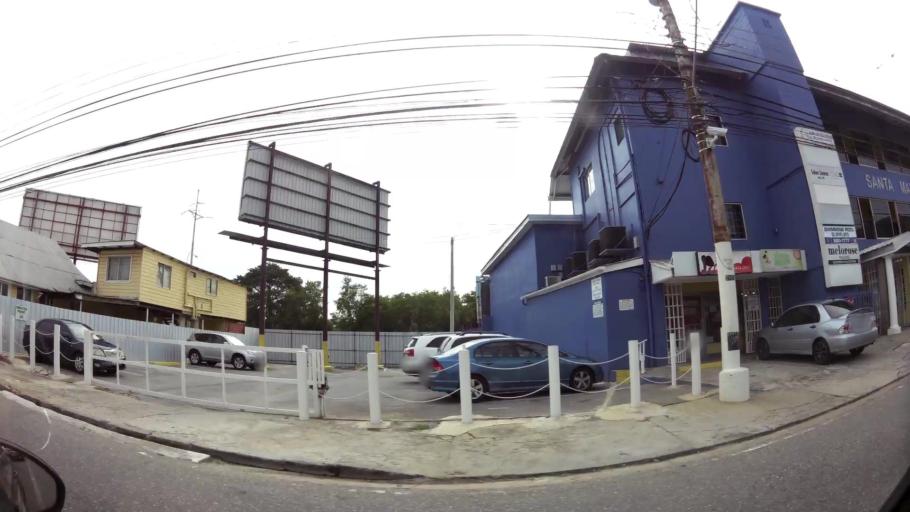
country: TT
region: City of Port of Spain
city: Mucurapo
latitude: 10.6688
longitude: -61.5365
